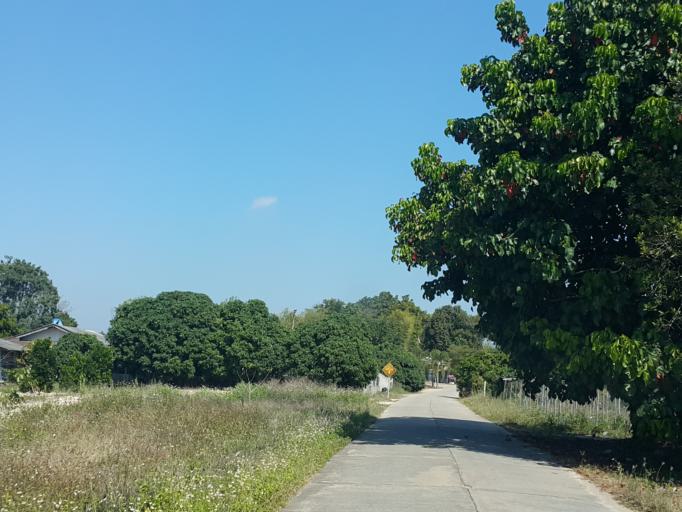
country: TH
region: Chiang Mai
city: Mae Taeng
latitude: 18.9926
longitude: 98.9812
